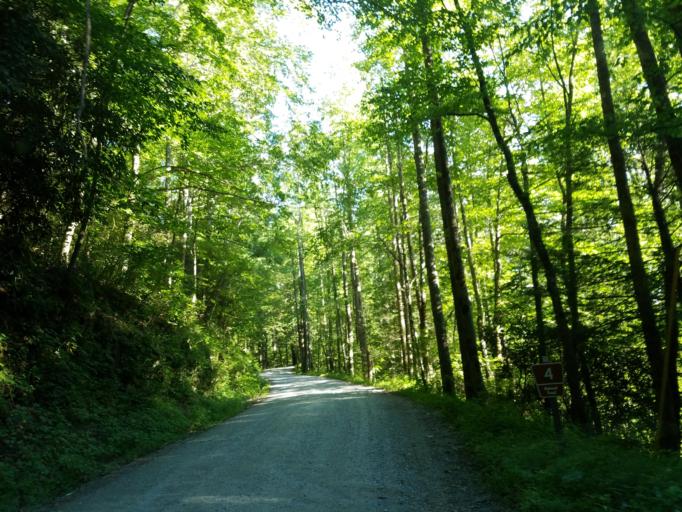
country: US
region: Georgia
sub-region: Union County
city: Blairsville
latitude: 34.7639
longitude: -84.0953
